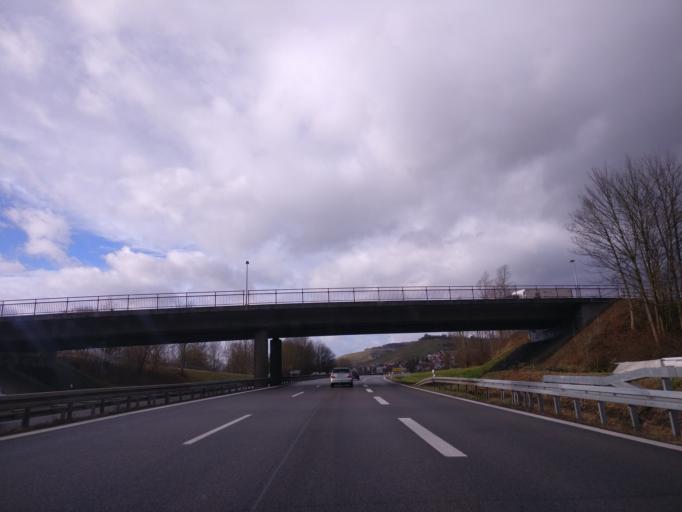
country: DE
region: Baden-Wuerttemberg
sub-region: Regierungsbezirk Stuttgart
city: Winterbach
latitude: 48.8091
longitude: 9.4347
